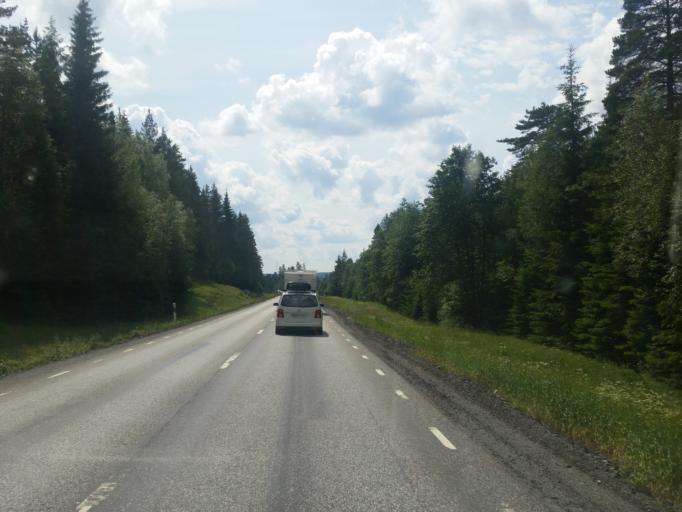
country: SE
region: OErebro
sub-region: Ljusnarsbergs Kommun
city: Kopparberg
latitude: 59.8991
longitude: 15.0189
